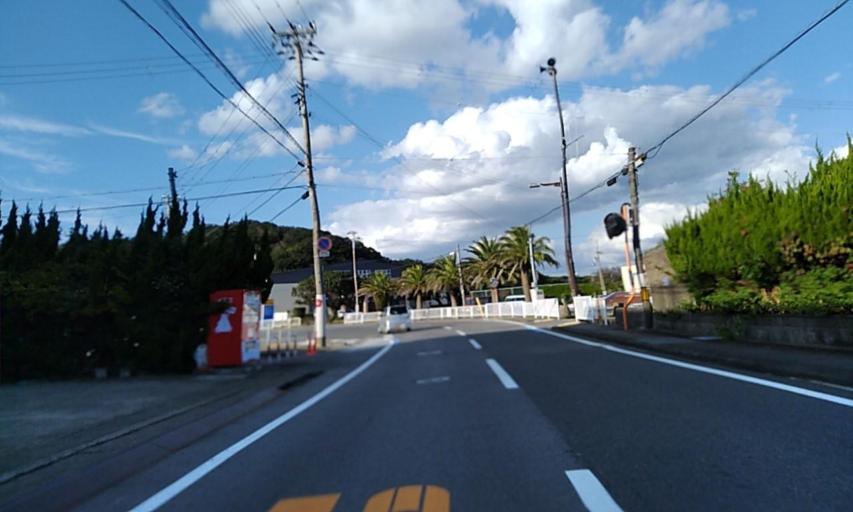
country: JP
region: Wakayama
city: Tanabe
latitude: 33.6919
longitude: 135.3553
